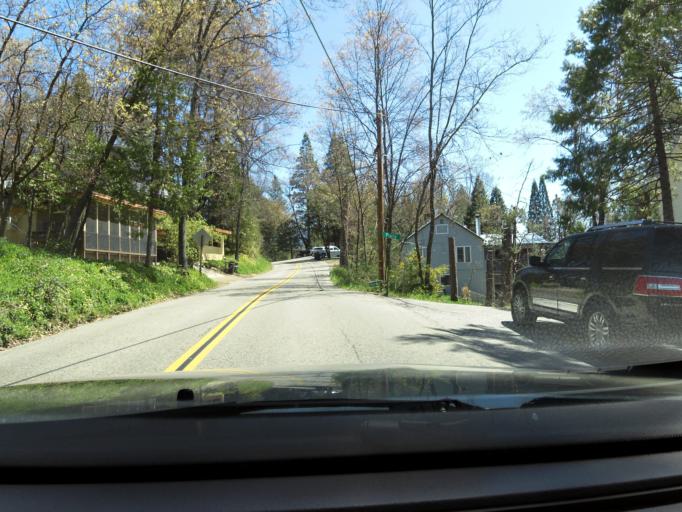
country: US
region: California
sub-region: Madera County
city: Oakhurst
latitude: 37.3208
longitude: -119.5620
